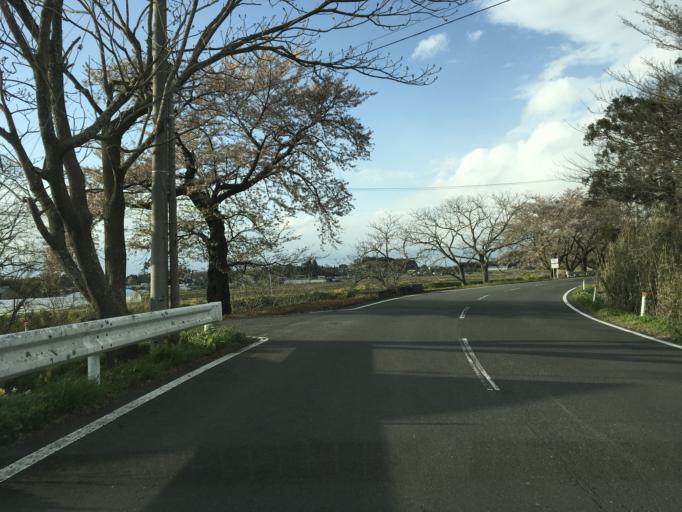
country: JP
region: Miyagi
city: Wakuya
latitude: 38.6499
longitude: 141.1442
